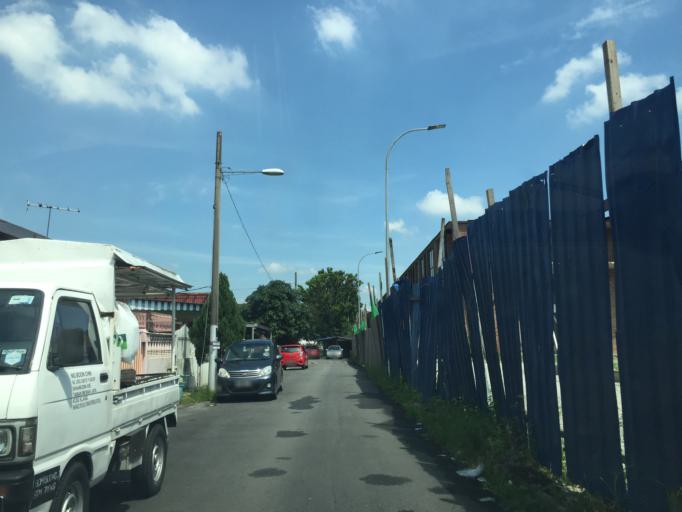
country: MY
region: Selangor
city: Klang
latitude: 3.0069
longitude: 101.4705
